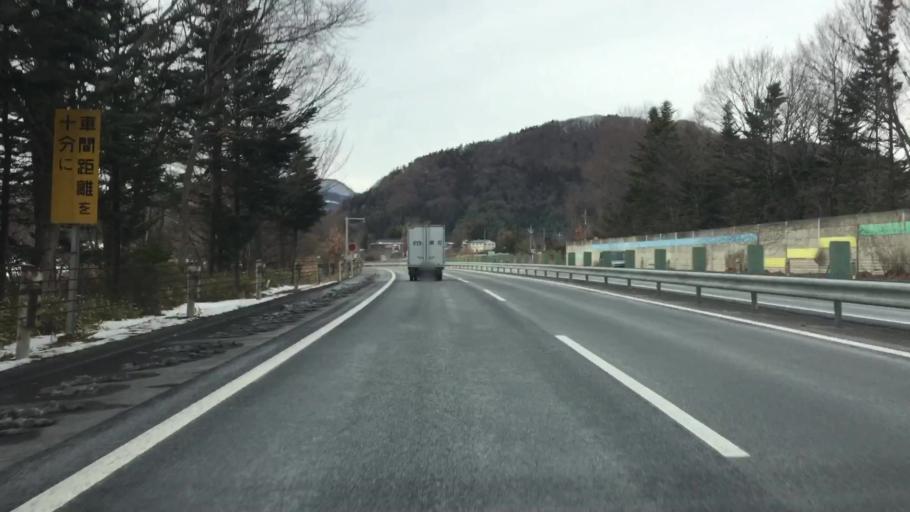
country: JP
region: Gunma
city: Numata
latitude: 36.6875
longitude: 139.0047
